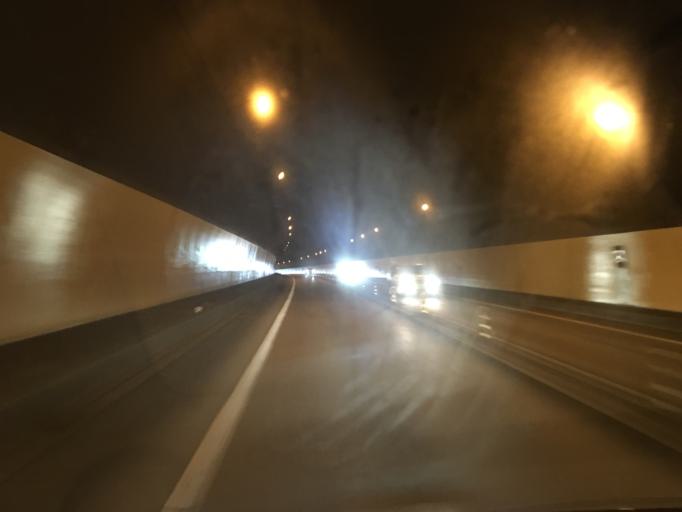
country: JP
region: Miyagi
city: Wakuya
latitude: 38.6320
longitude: 141.2811
